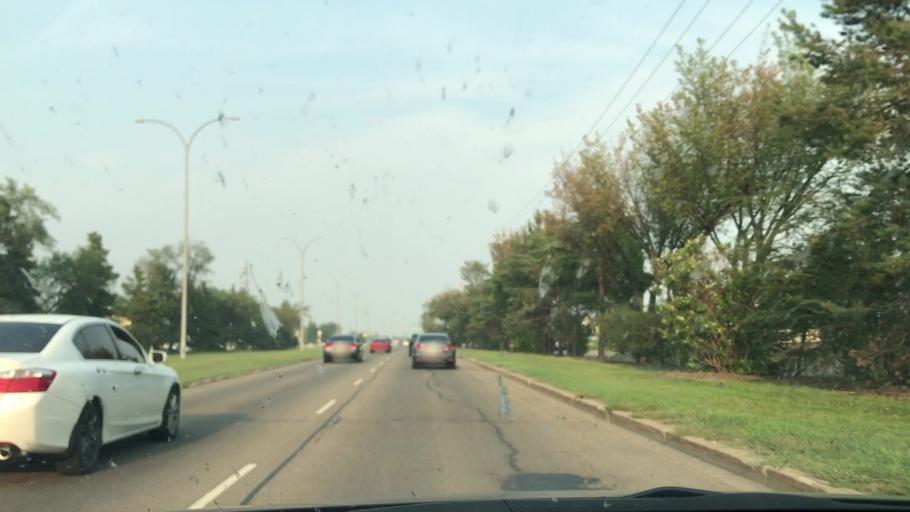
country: CA
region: Alberta
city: Edmonton
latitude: 53.5996
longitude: -113.4526
